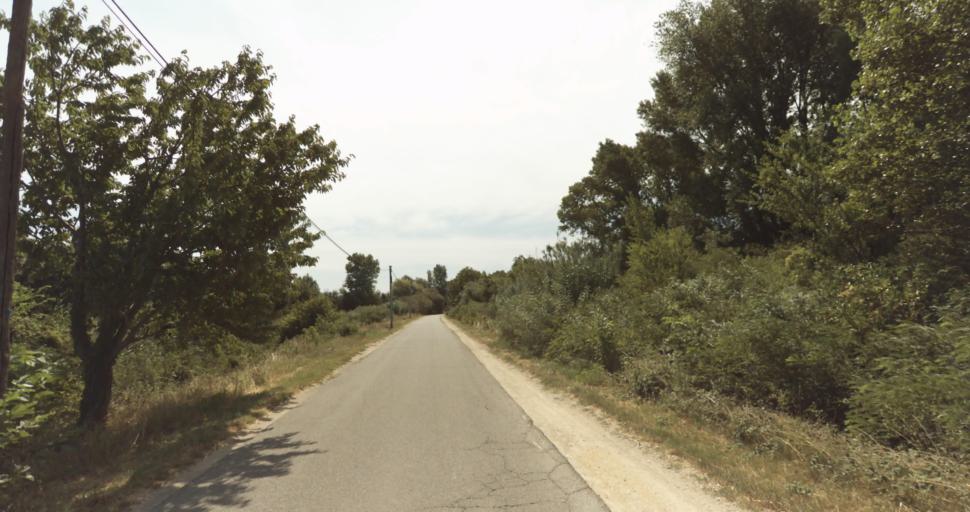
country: FR
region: Provence-Alpes-Cote d'Azur
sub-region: Departement du Vaucluse
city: Monteux
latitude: 44.0181
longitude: 4.9794
